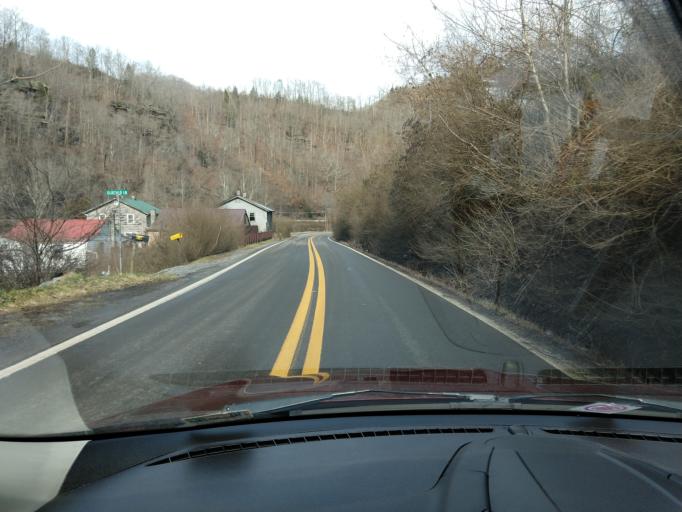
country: US
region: West Virginia
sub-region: McDowell County
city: Welch
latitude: 37.3394
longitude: -81.7212
